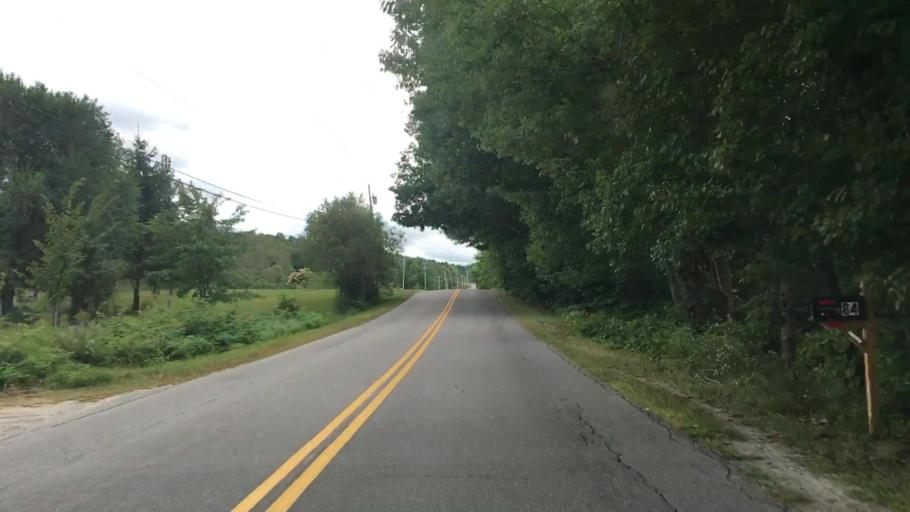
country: US
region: Maine
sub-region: Kennebec County
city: Hallowell
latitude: 44.2734
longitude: -69.8116
